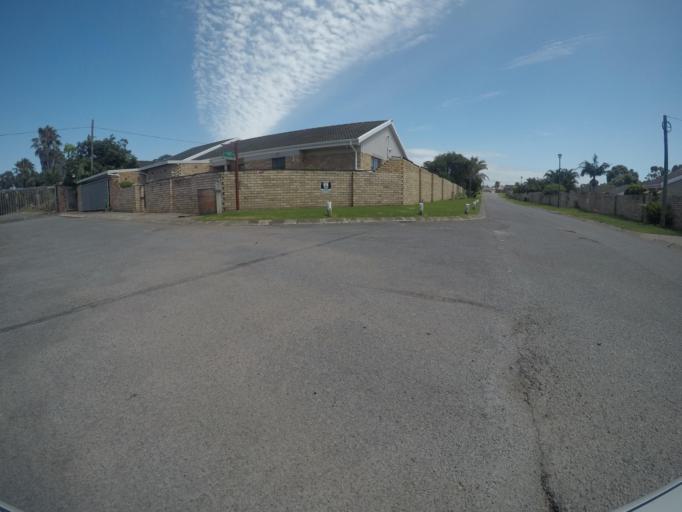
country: ZA
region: Eastern Cape
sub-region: Buffalo City Metropolitan Municipality
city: East London
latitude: -32.9512
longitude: 28.0003
